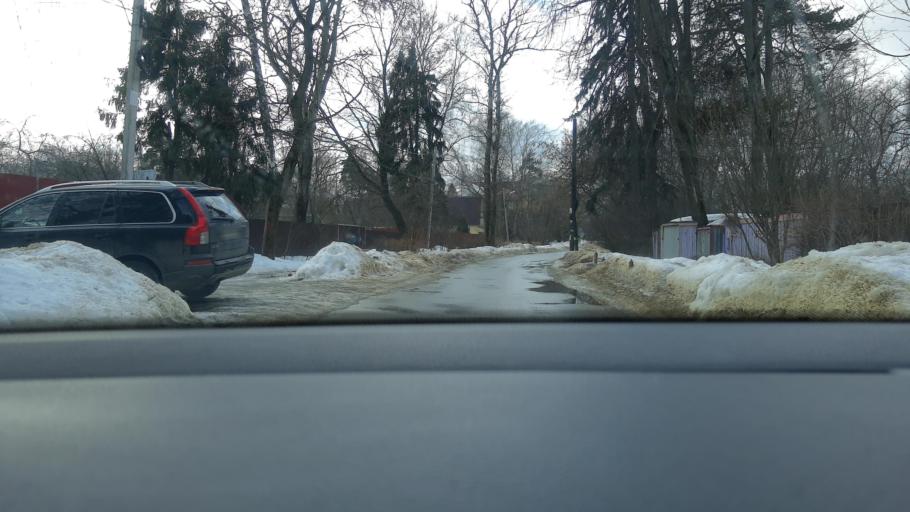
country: RU
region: Moskovskaya
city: Druzhba
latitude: 55.8946
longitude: 37.7362
